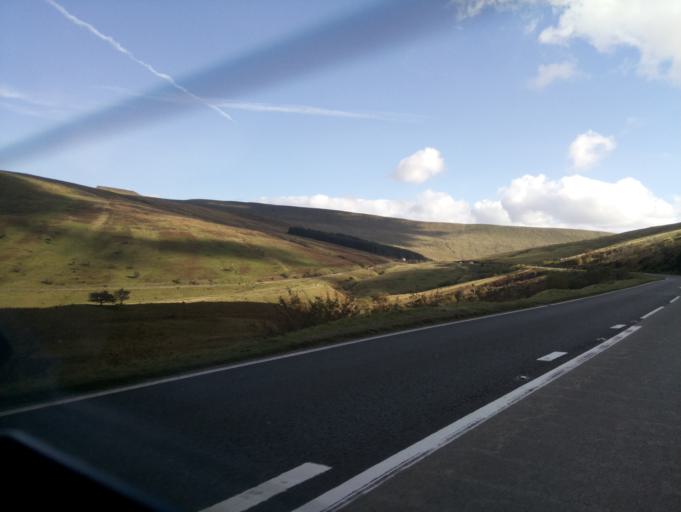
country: GB
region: Wales
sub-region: Sir Powys
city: Cray
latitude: 51.8760
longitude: -3.4939
